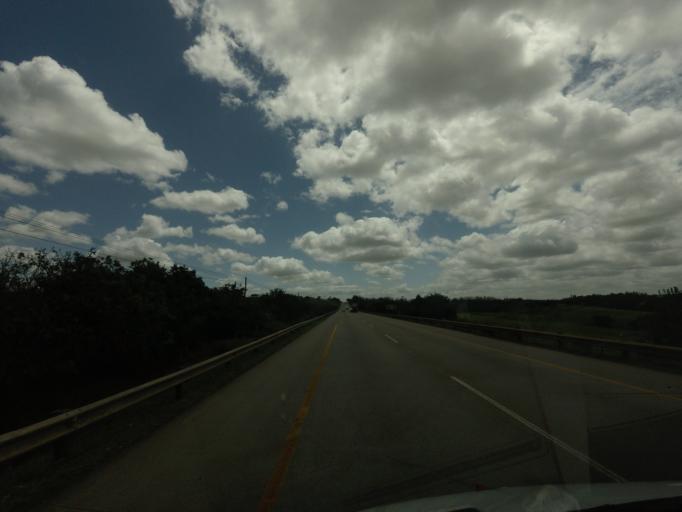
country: ZA
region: KwaZulu-Natal
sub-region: uMkhanyakude District Municipality
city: Mtubatuba
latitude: -28.4833
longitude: 32.1428
